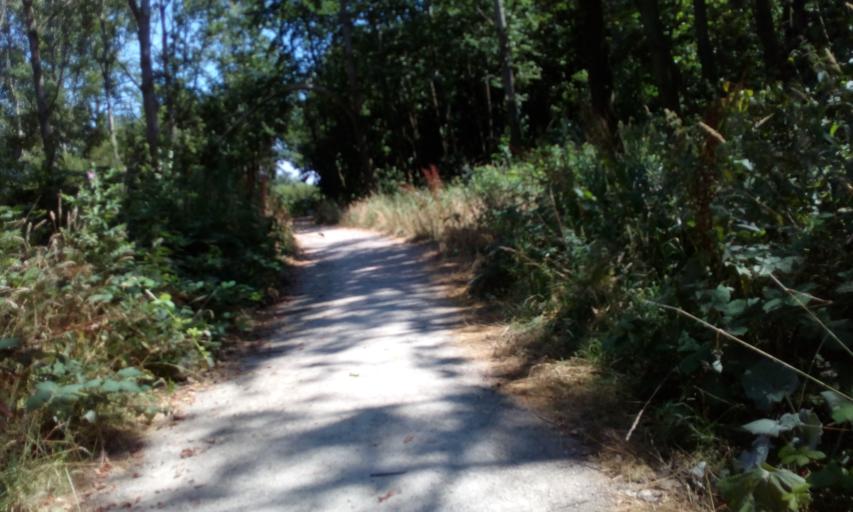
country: NL
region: South Holland
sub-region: Gemeente Pijnacker-Nootdorp
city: Pijnacker
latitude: 52.0337
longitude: 4.4183
